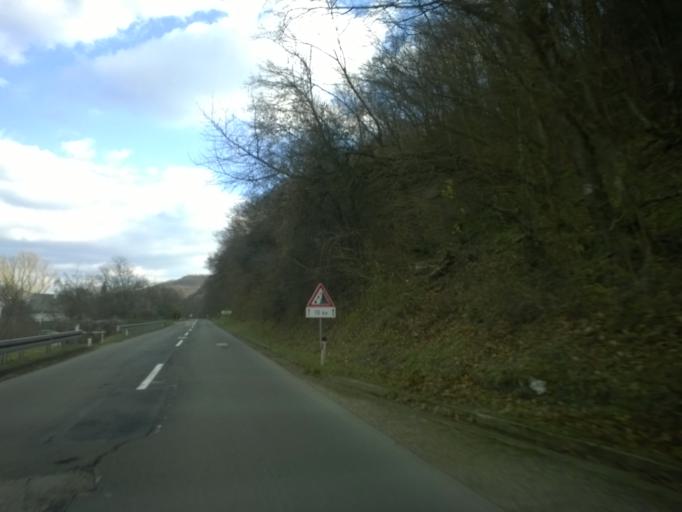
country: RO
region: Caras-Severin
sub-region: Comuna Berzasca
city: Liubcova
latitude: 44.6420
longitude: 21.8927
